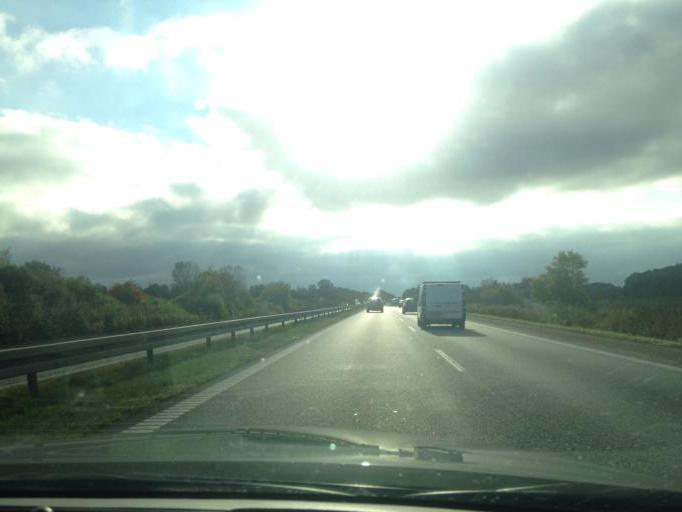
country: DK
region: South Denmark
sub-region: Fredericia Kommune
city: Taulov
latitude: 55.5771
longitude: 9.5700
